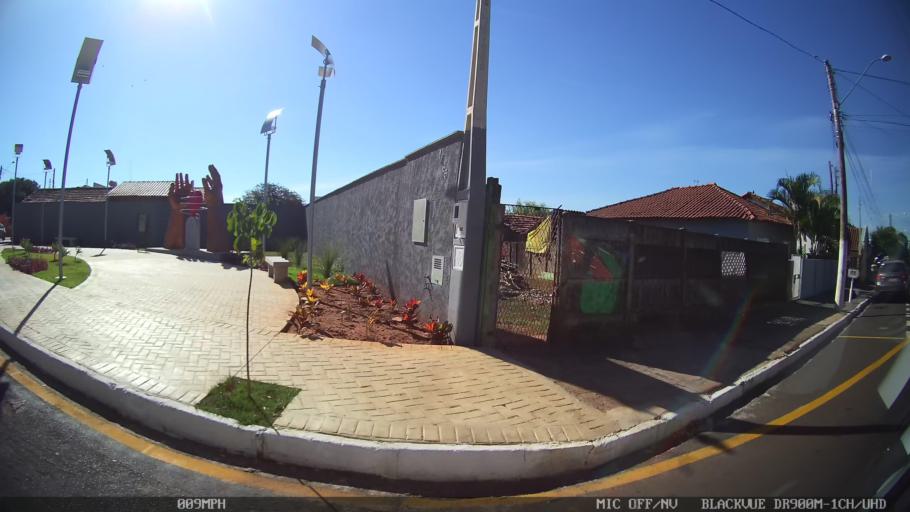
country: BR
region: Sao Paulo
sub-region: Olimpia
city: Olimpia
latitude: -20.7477
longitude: -48.9144
